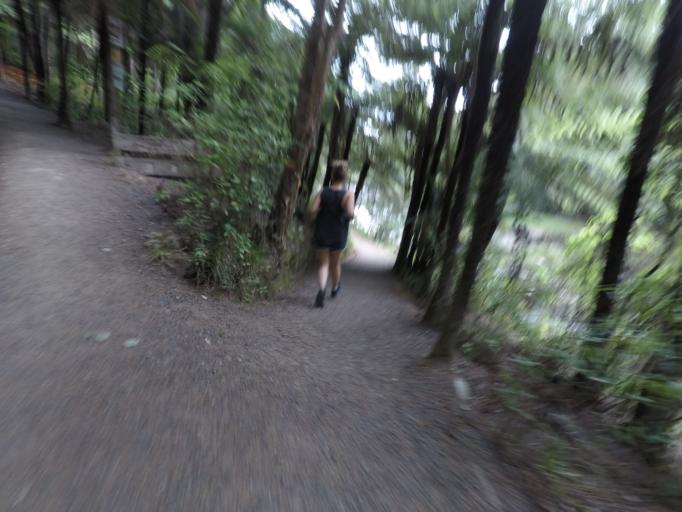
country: NZ
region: Northland
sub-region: Whangarei
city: Whangarei
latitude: -35.7112
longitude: 174.3301
